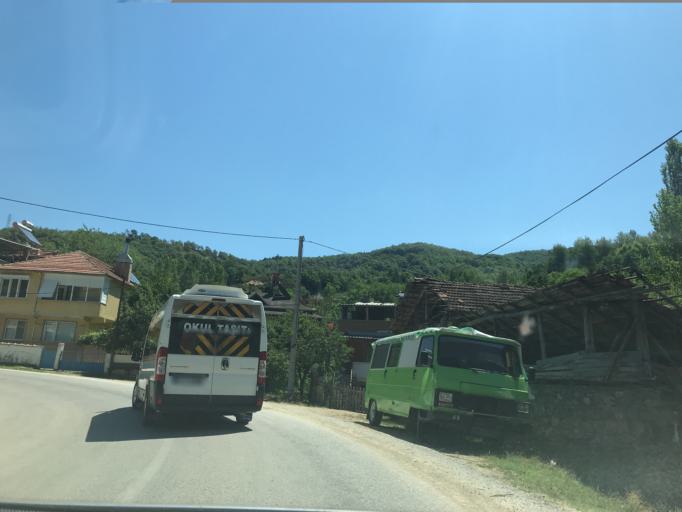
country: TR
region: Bursa
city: Tahtakopru
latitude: 39.9467
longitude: 29.5935
